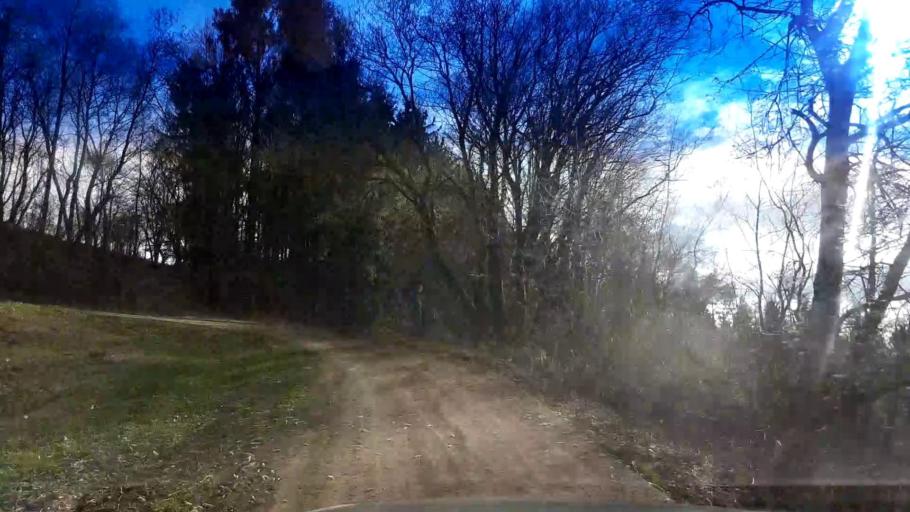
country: DE
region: Bavaria
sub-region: Upper Franconia
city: Schesslitz
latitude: 50.0092
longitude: 11.0352
